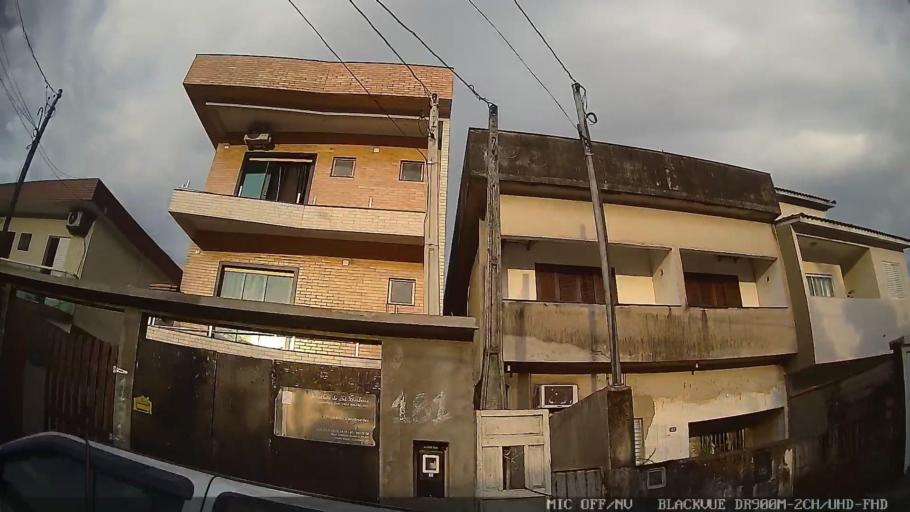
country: BR
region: Sao Paulo
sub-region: Cubatao
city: Cubatao
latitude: -23.8938
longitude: -46.4274
